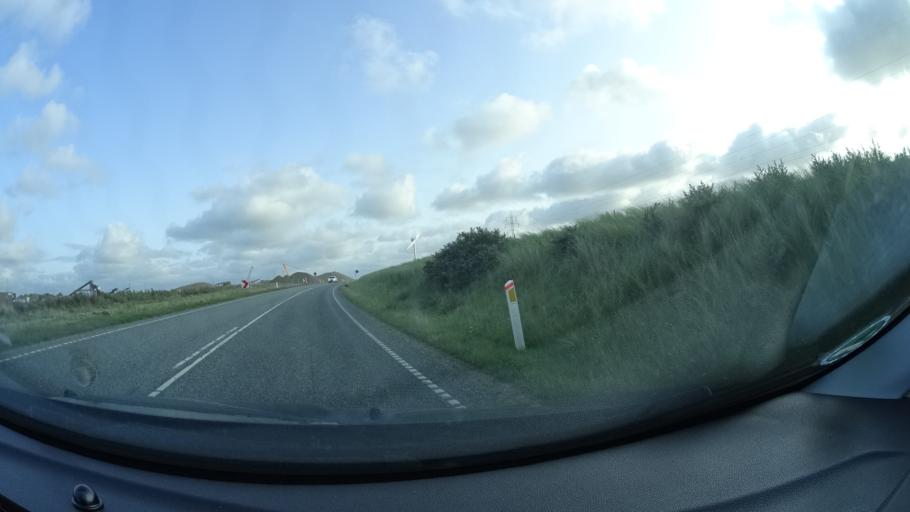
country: DK
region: Central Jutland
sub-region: Lemvig Kommune
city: Thyboron
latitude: 56.6836
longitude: 8.2238
